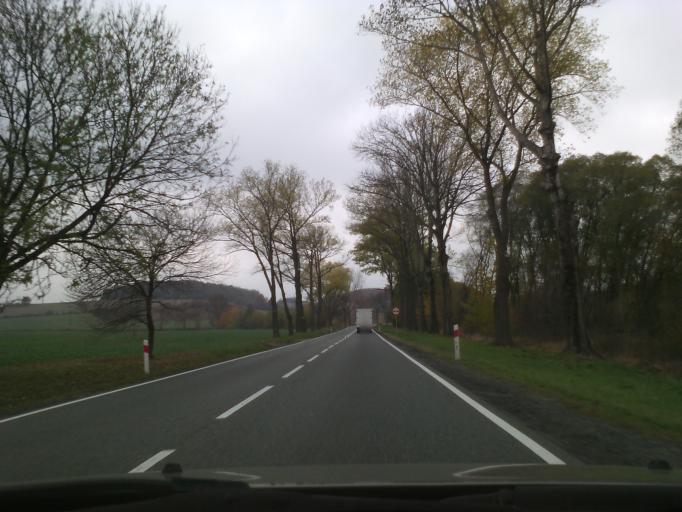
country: PL
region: Lower Silesian Voivodeship
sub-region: Powiat jaworski
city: Bolkow
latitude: 50.9165
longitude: 16.1177
